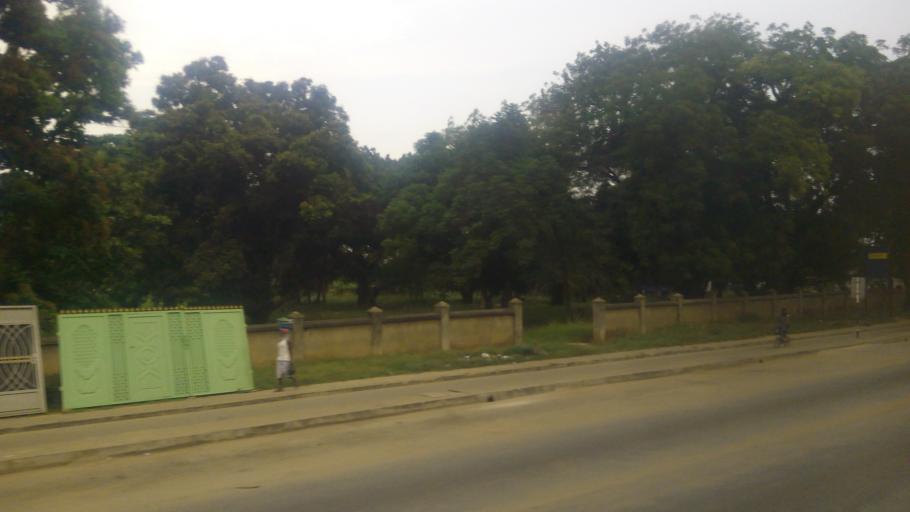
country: GH
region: Western
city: Takoradi
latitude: 4.9061
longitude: -1.7744
